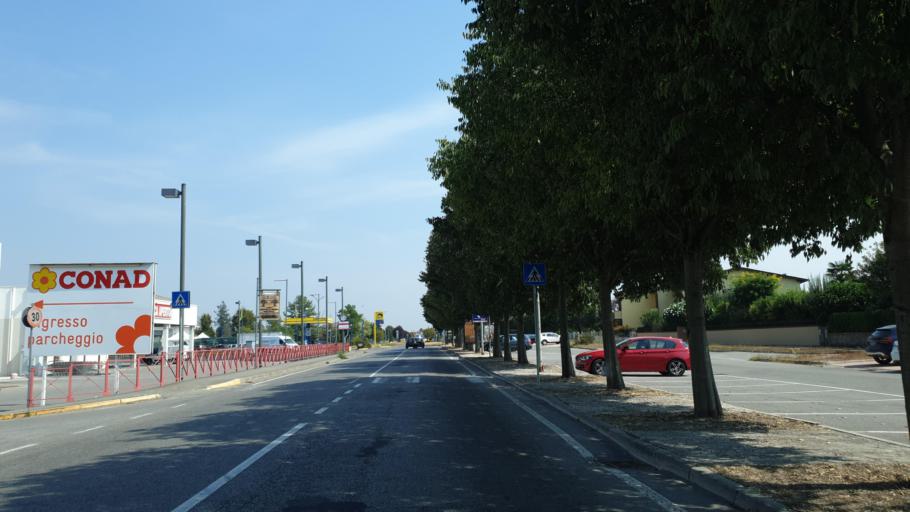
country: IT
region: Lombardy
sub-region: Provincia di Brescia
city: Leno
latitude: 45.3648
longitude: 10.2065
